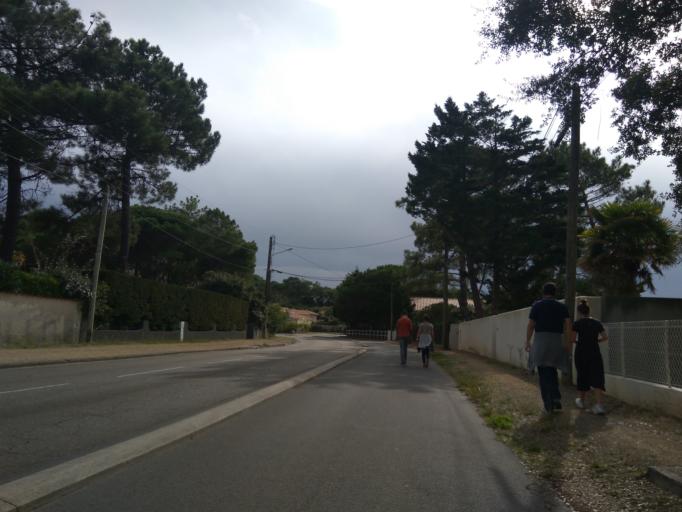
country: FR
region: Aquitaine
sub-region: Departement des Landes
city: Capbreton
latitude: 43.6423
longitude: -1.4415
